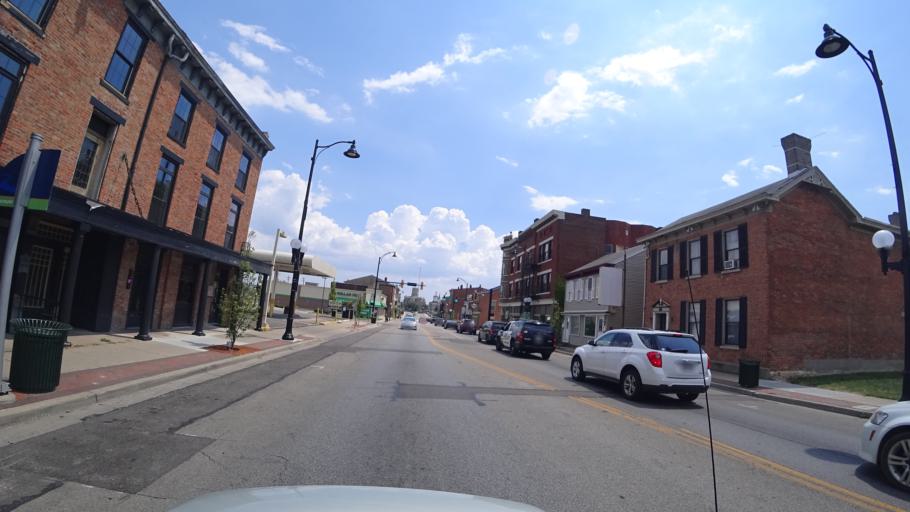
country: US
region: Ohio
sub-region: Butler County
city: Hamilton
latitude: 39.4035
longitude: -84.5685
